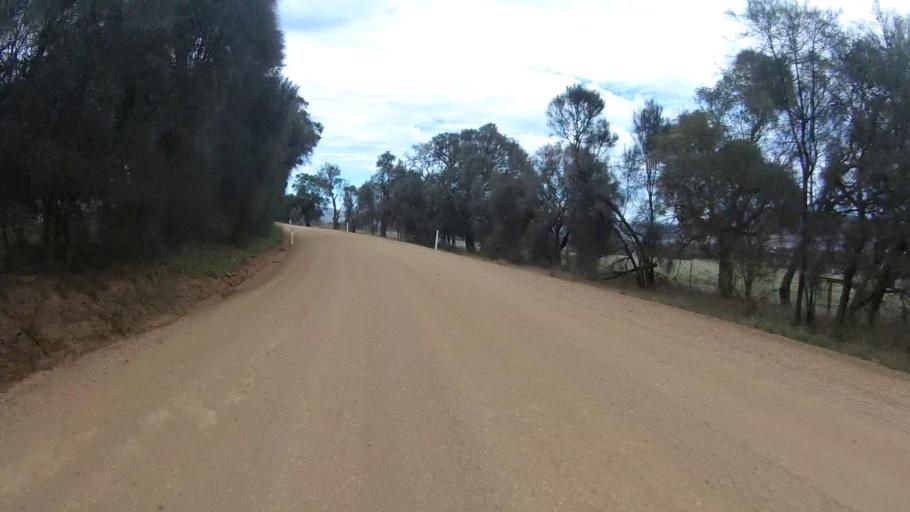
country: AU
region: Tasmania
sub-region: Sorell
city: Sorell
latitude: -42.7004
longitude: 147.4585
